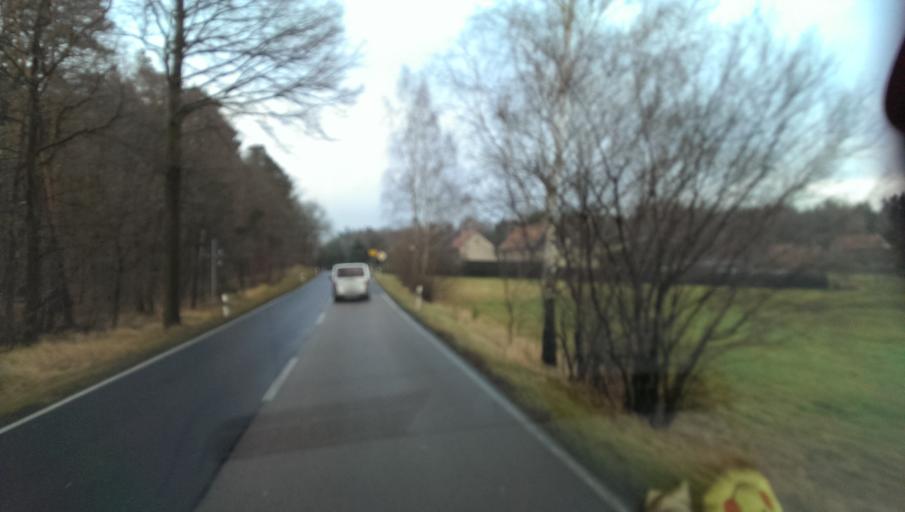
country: DE
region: Saxony
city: Weinbohla
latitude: 51.1770
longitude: 13.6184
